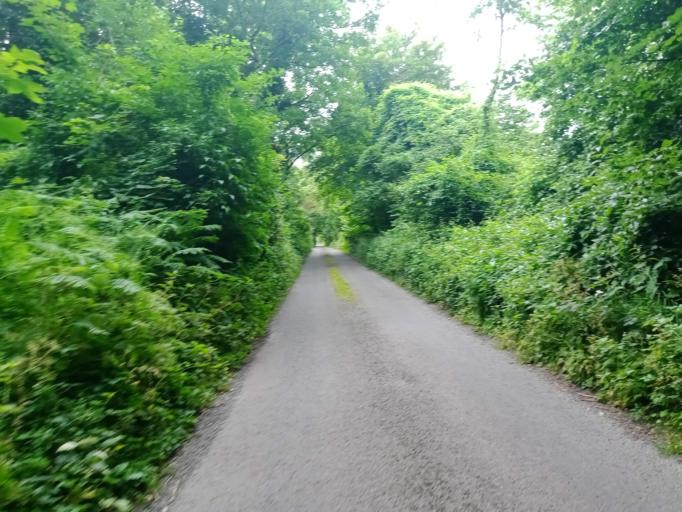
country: IE
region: Leinster
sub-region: Laois
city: Abbeyleix
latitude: 52.8991
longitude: -7.3610
